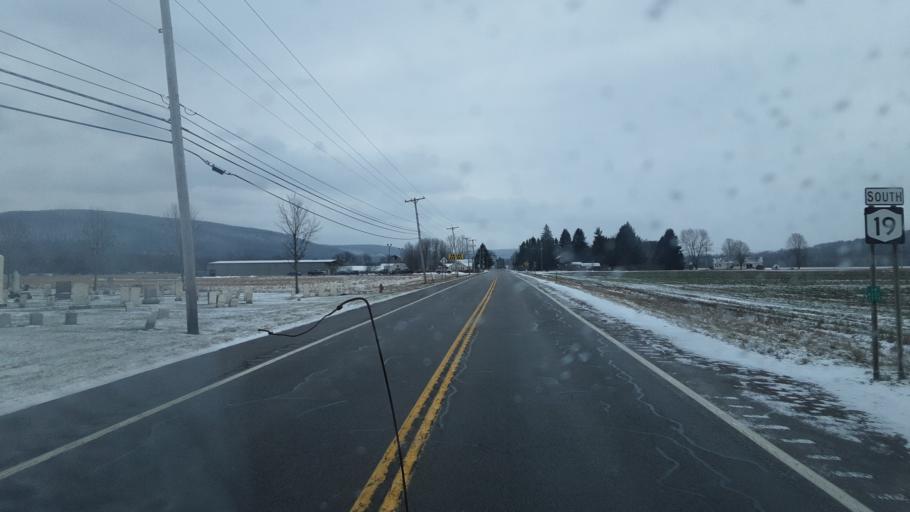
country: US
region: New York
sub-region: Allegany County
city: Belmont
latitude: 42.2108
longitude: -78.0168
